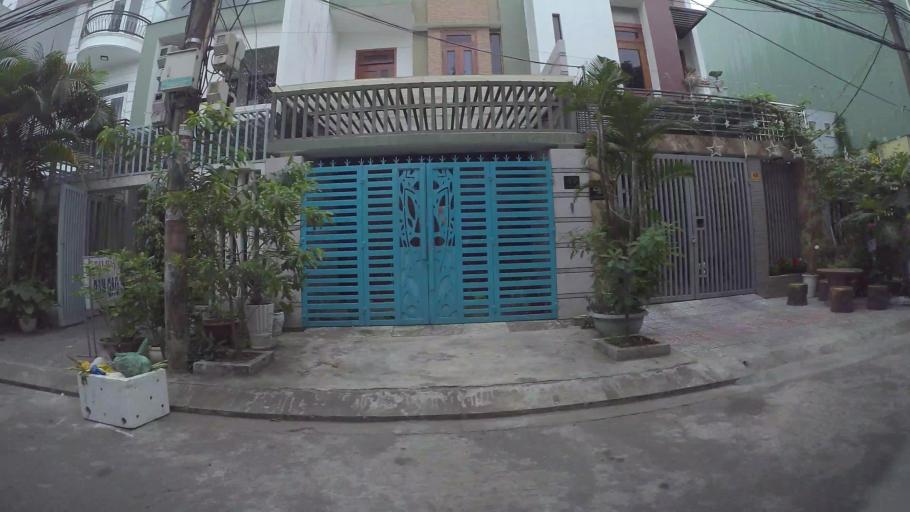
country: VN
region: Da Nang
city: Lien Chieu
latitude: 16.0733
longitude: 108.1726
